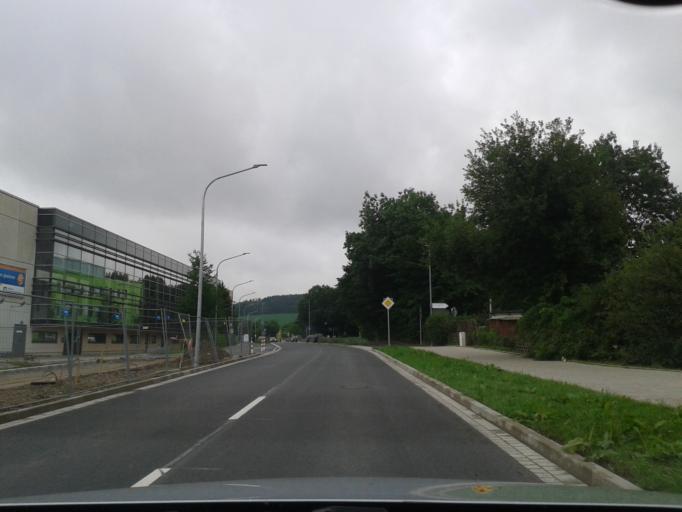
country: DE
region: North Rhine-Westphalia
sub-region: Regierungsbezirk Detmold
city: Lemgo
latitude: 52.0177
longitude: 8.9073
